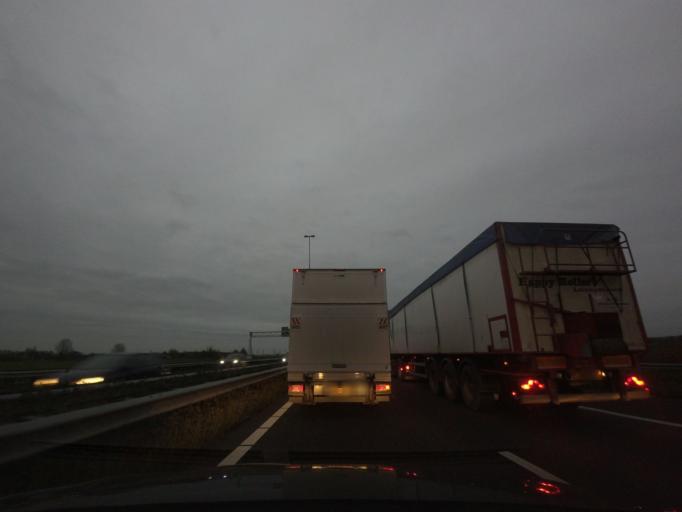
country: NL
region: North Brabant
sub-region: Gemeente Woudrichem
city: Almkerk
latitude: 51.7939
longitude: 4.9300
